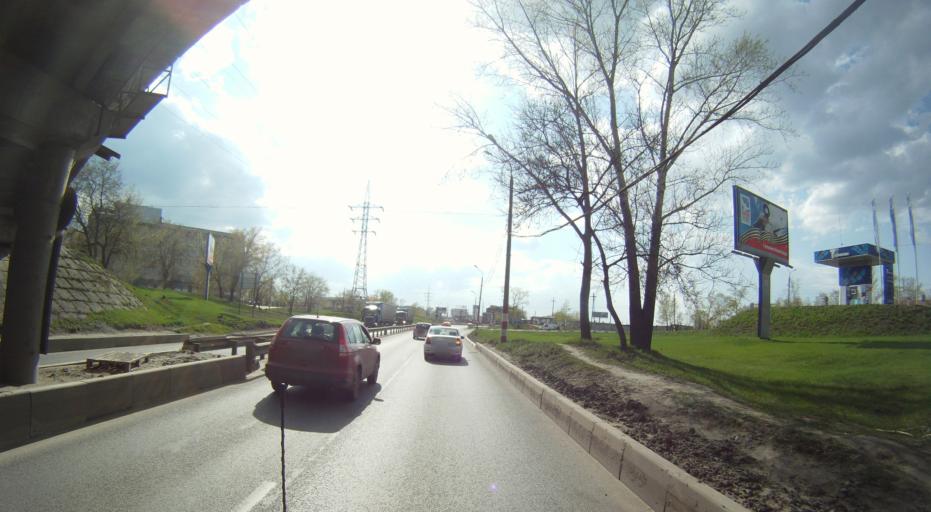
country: RU
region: Nizjnij Novgorod
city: Nizhniy Novgorod
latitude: 56.2964
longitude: 43.9360
